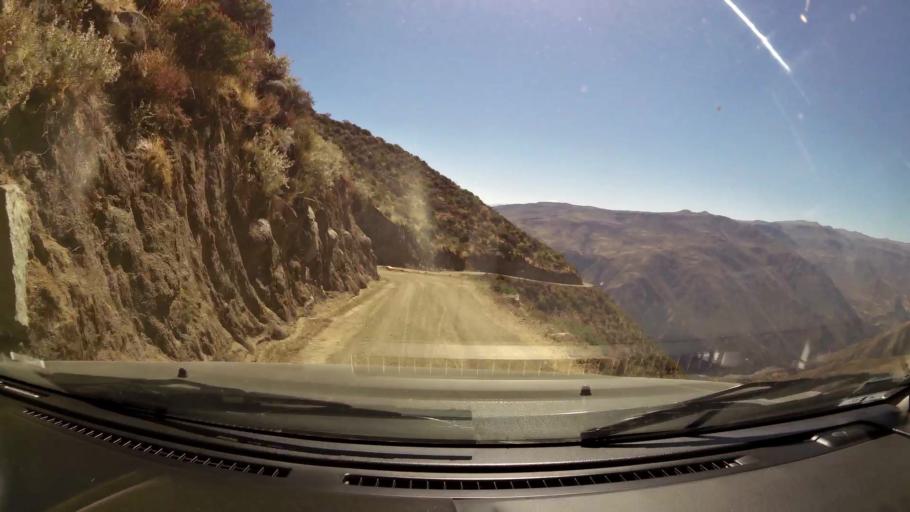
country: PE
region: Huancavelica
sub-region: Huaytara
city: Quito-Arma
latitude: -13.6223
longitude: -75.3508
